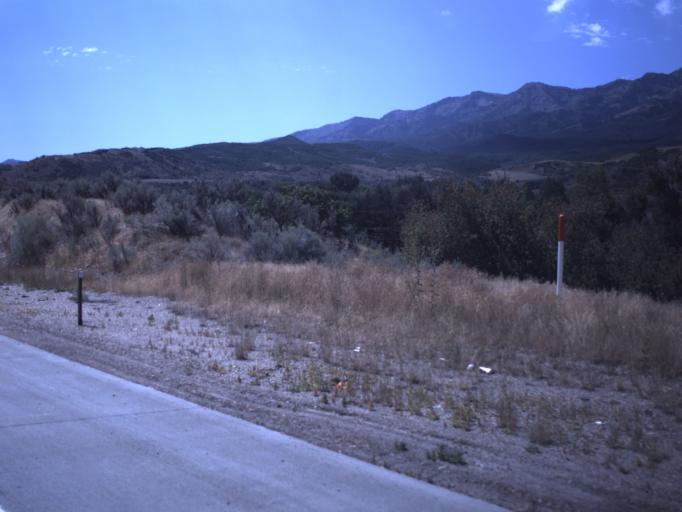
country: US
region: Utah
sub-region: Morgan County
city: Mountain Green
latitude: 41.1224
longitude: -111.7652
